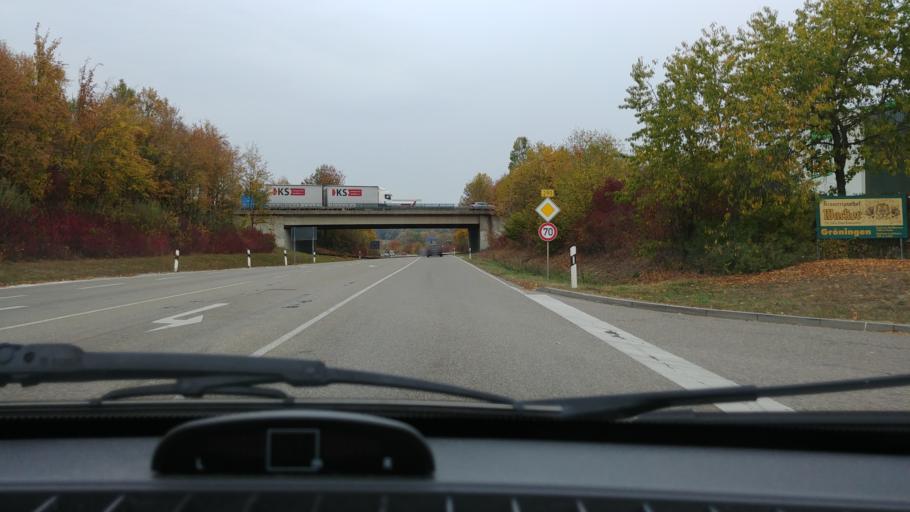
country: DE
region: Baden-Wuerttemberg
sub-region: Regierungsbezirk Stuttgart
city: Satteldorf
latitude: 49.1823
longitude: 10.0717
